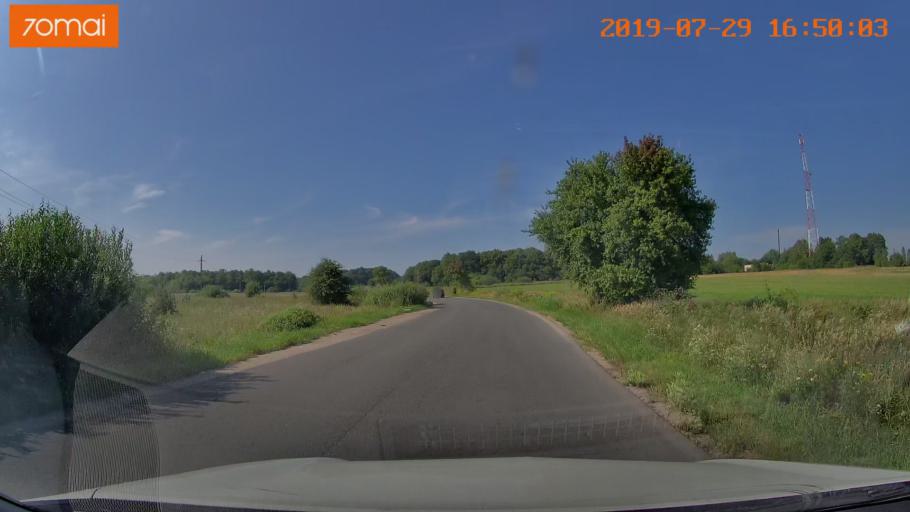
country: RU
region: Kaliningrad
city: Primorsk
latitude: 54.7998
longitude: 20.0582
